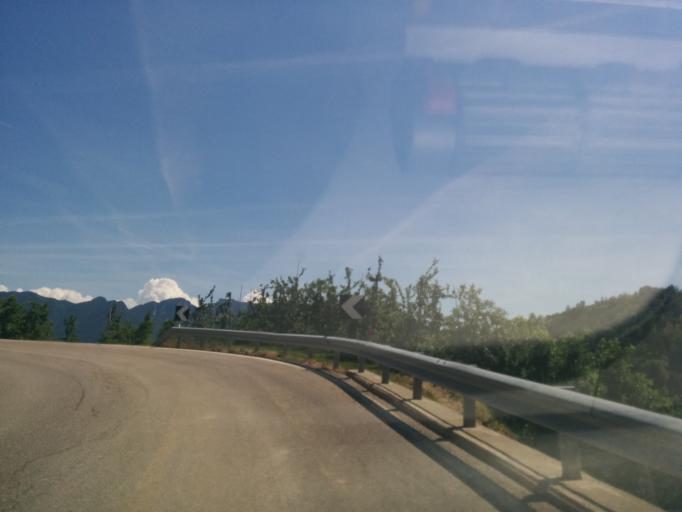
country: IT
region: Trentino-Alto Adige
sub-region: Provincia di Trento
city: Terres
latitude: 46.3183
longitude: 11.0194
